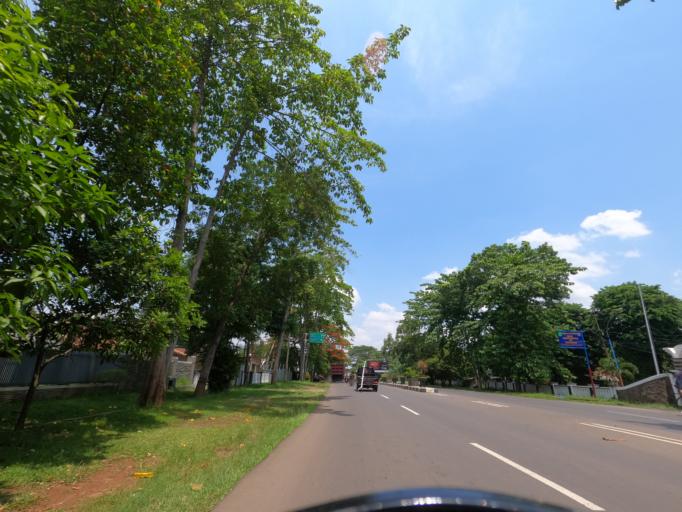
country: ID
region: West Java
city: Pamanukan
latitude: -6.5516
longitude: 107.7644
